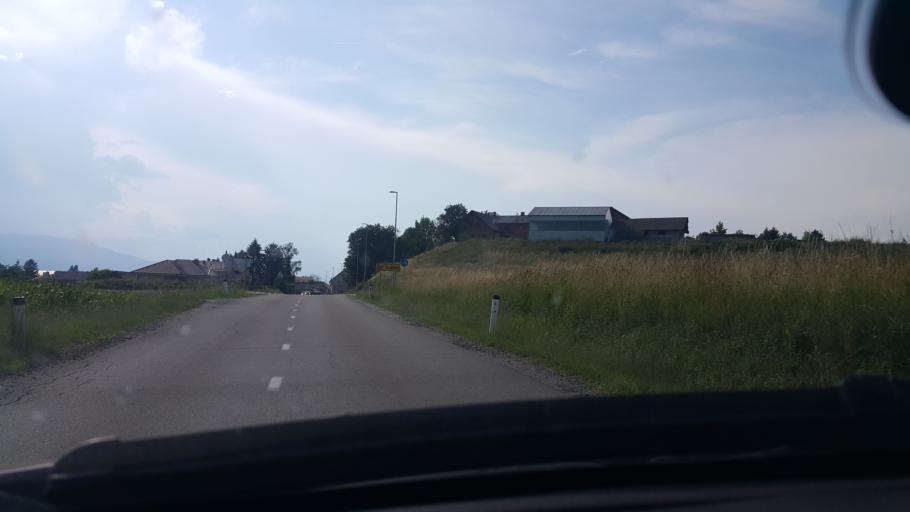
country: SI
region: Duplek
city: Spodnji Duplek
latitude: 46.4997
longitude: 15.7596
